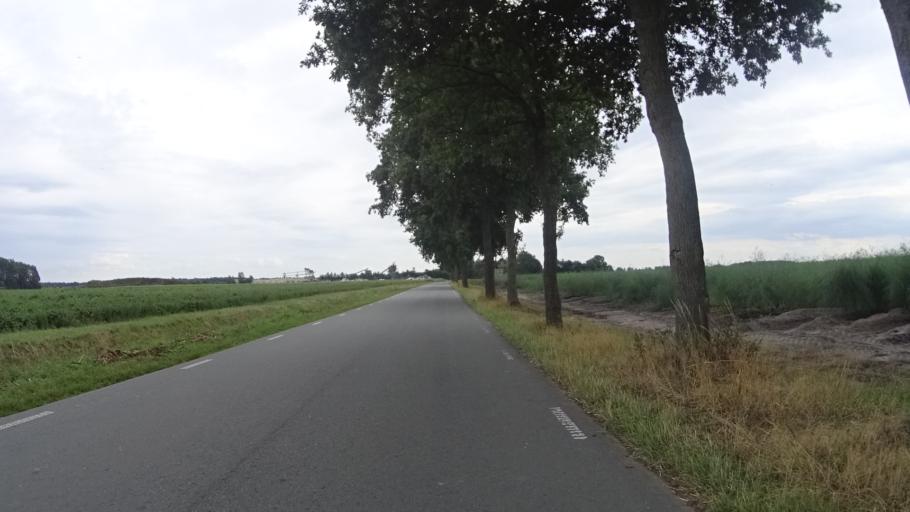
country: NL
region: Groningen
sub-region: Gemeente Slochteren
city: Slochteren
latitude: 53.1910
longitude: 6.8507
